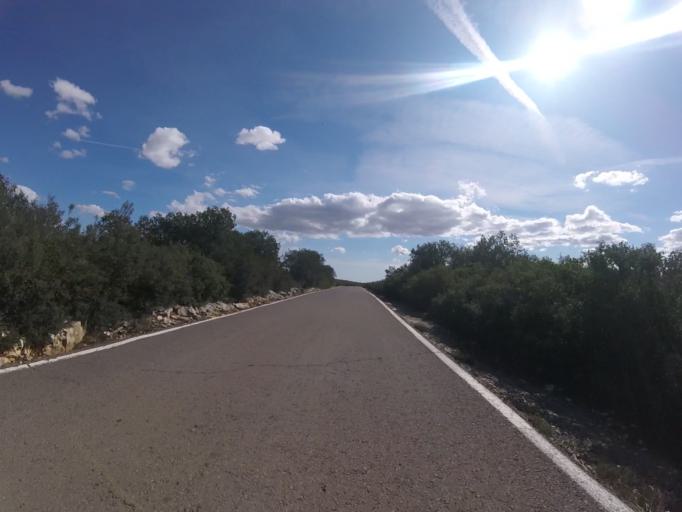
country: ES
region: Valencia
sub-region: Provincia de Castello
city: Albocasser
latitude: 40.3984
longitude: 0.0874
